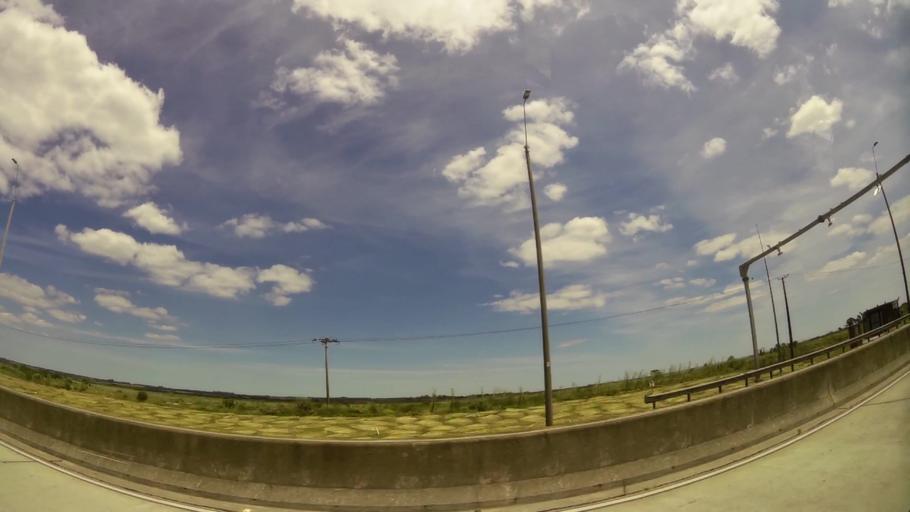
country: UY
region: San Jose
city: Delta del Tigre
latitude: -34.7742
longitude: -56.3796
